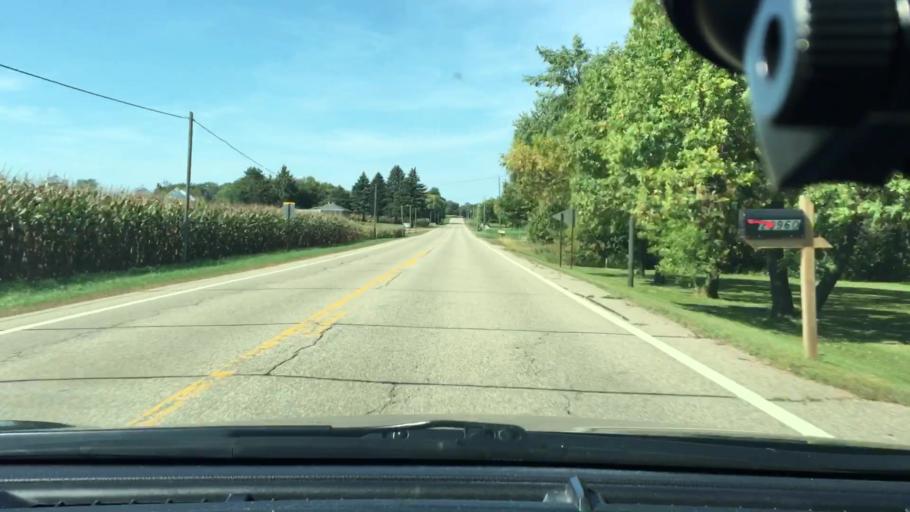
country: US
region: Minnesota
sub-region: Hennepin County
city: Corcoran
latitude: 45.1123
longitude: -93.5731
